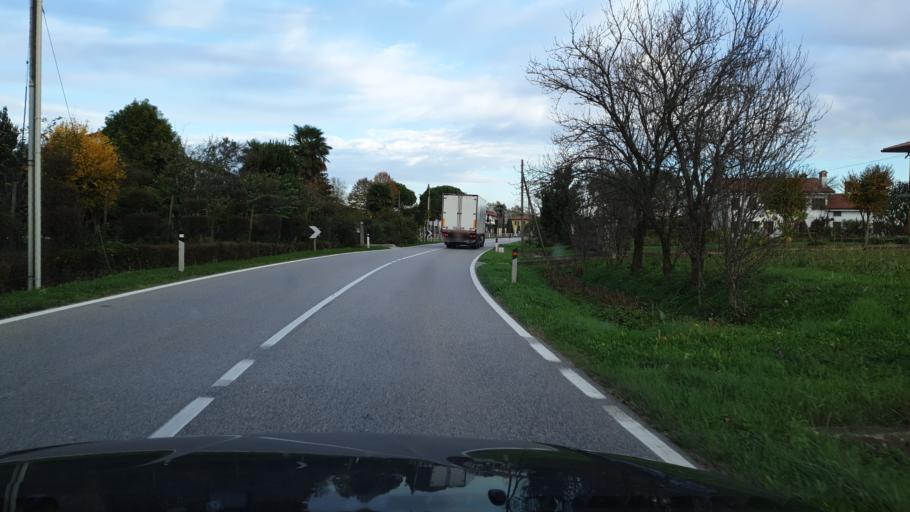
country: IT
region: Veneto
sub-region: Provincia di Padova
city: Pernumia
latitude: 45.2325
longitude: 11.7833
